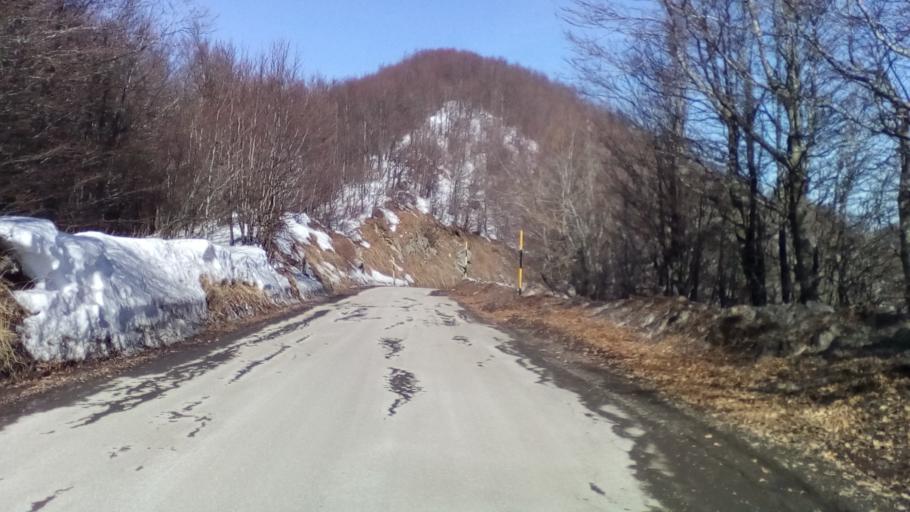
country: IT
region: Tuscany
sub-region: Provincia di Lucca
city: Castiglione di Garfagnana
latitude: 44.2018
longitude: 10.4875
